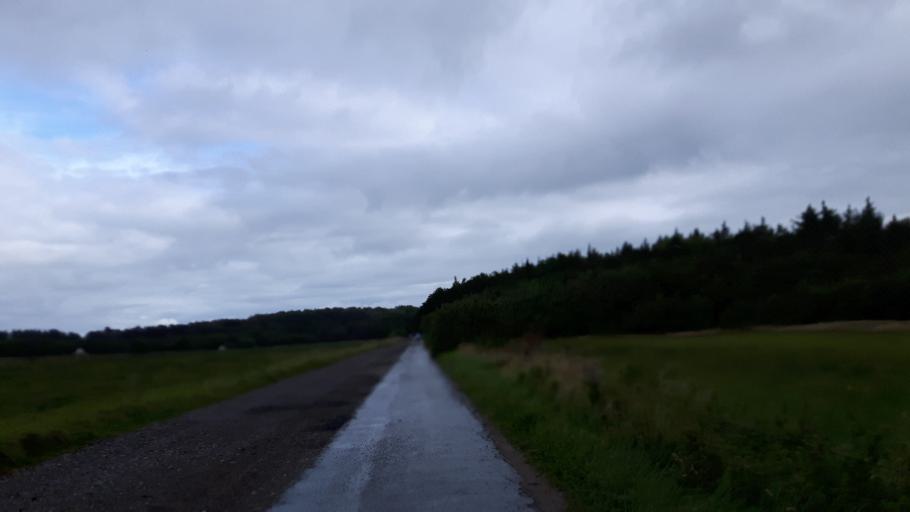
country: NL
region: Friesland
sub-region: Gemeente Ameland
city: Nes
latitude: 53.4490
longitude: 5.7573
